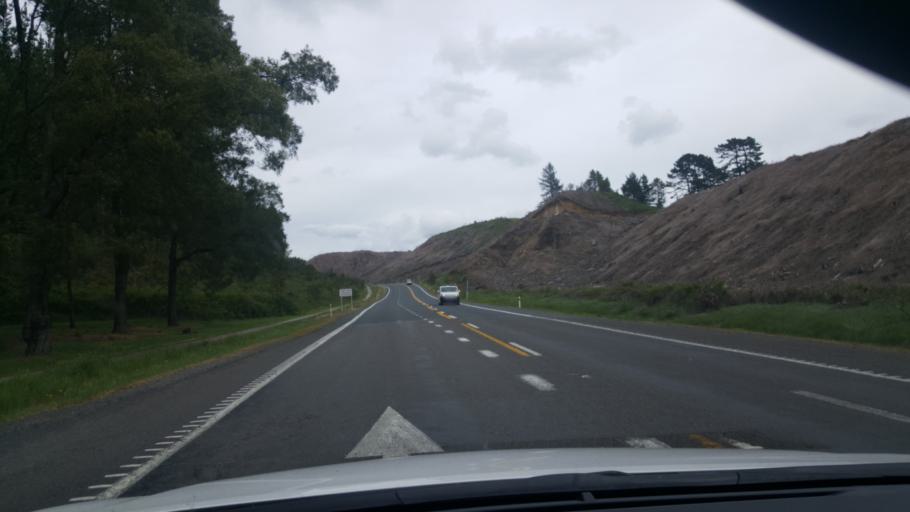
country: NZ
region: Bay of Plenty
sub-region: Rotorua District
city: Rotorua
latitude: -38.2303
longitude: 176.2977
